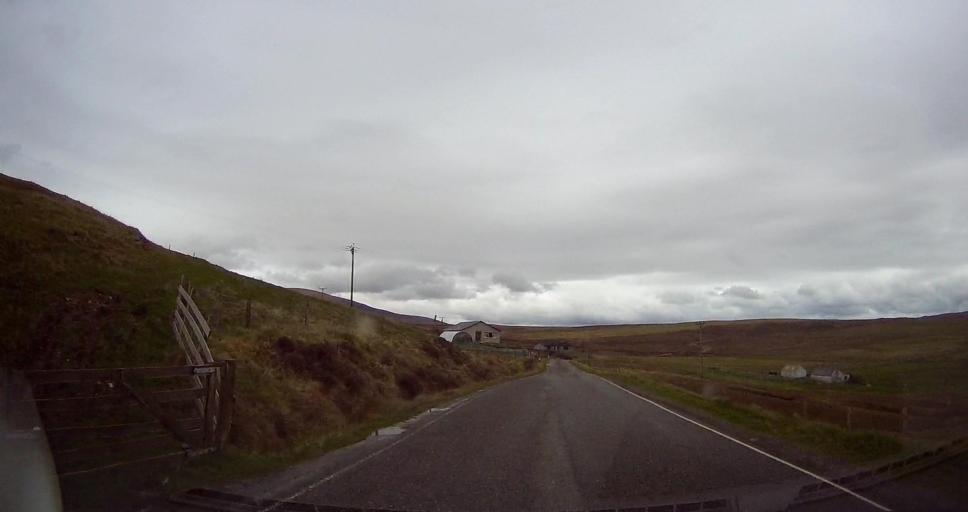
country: GB
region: Scotland
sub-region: Shetland Islands
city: Lerwick
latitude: 60.4871
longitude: -1.4967
